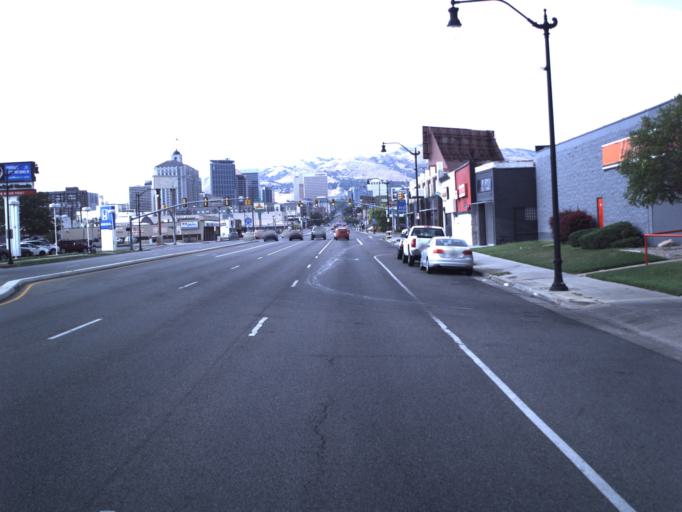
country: US
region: Utah
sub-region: Salt Lake County
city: Salt Lake City
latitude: 40.7484
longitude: -111.8881
